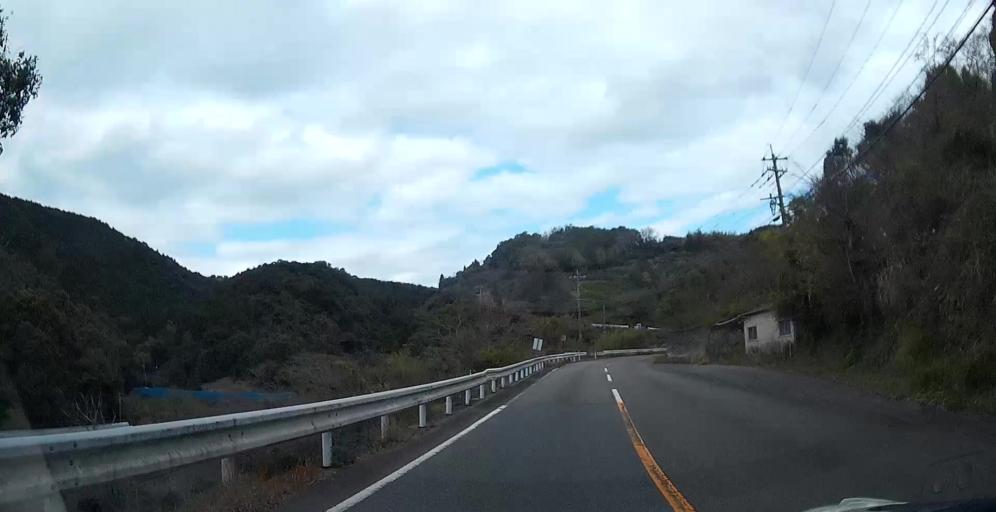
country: JP
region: Kumamoto
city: Yatsushiro
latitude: 32.3658
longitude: 130.5065
